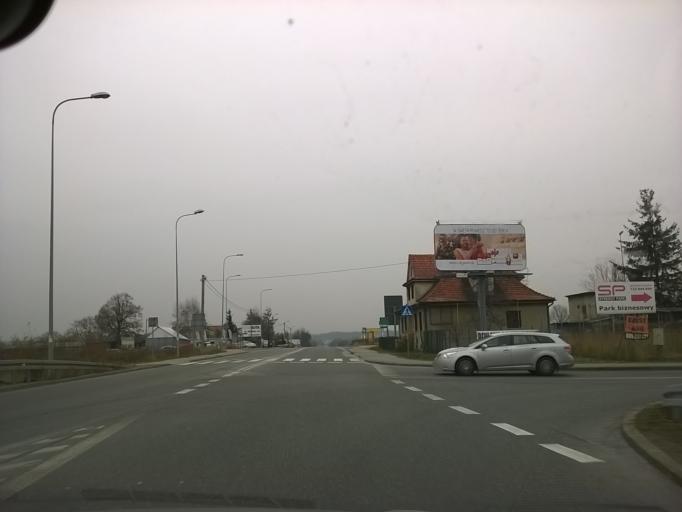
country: PL
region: Silesian Voivodeship
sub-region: Powiat gliwicki
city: Przyszowice
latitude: 50.2595
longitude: 18.7263
